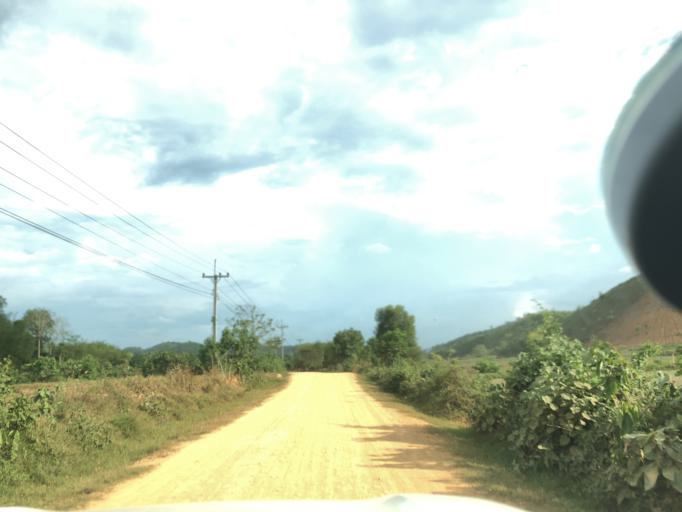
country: TH
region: Loei
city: Chiang Khan
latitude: 18.0079
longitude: 101.4204
